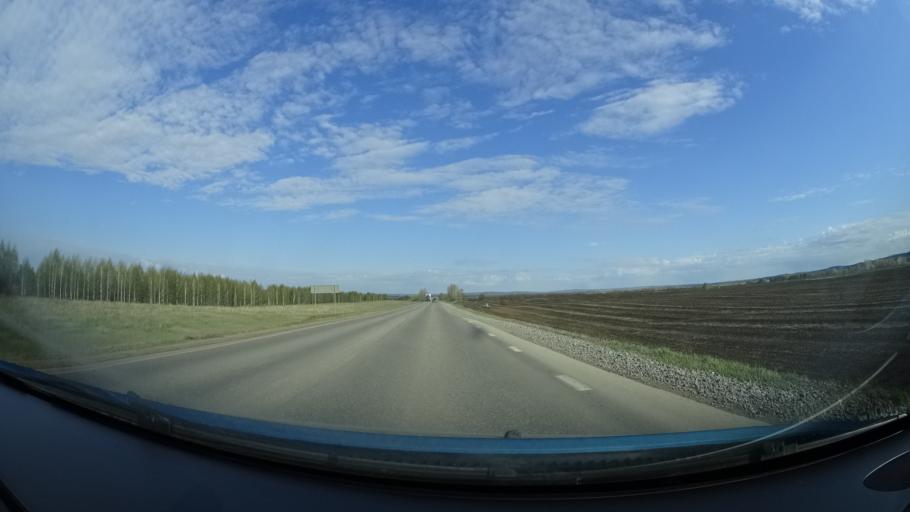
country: RU
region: Bashkortostan
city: Blagoveshchensk
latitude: 55.1883
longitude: 55.8435
